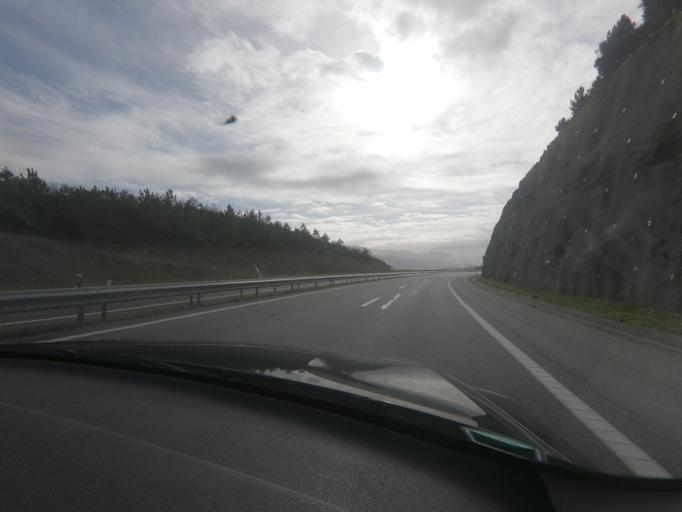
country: PT
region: Vila Real
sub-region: Santa Marta de Penaguiao
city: Santa Marta de Penaguiao
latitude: 41.2119
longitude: -7.7353
